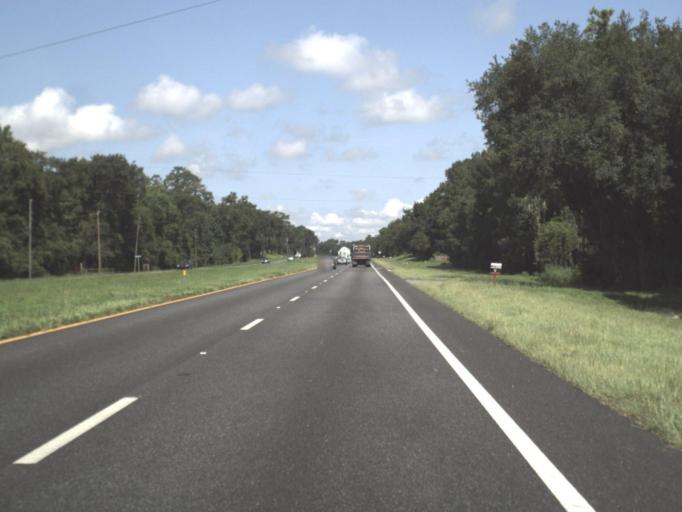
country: US
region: Florida
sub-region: Hernando County
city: Hill 'n Dale
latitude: 28.5325
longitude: -82.3299
